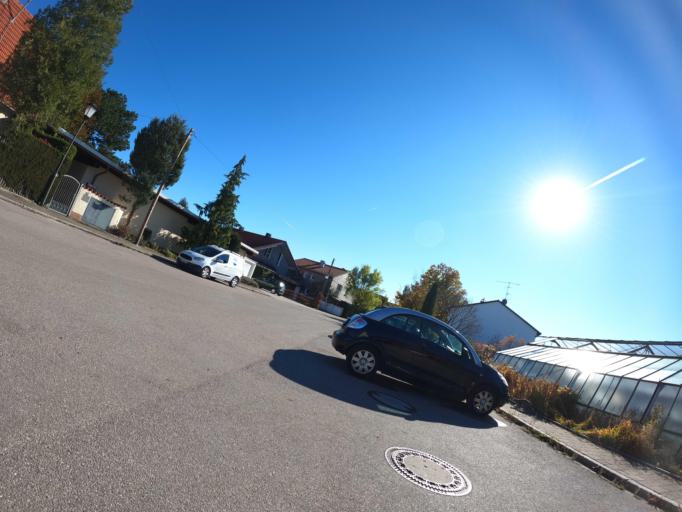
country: DE
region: Bavaria
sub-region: Upper Bavaria
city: Feldkirchen
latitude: 48.1320
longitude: 11.7353
